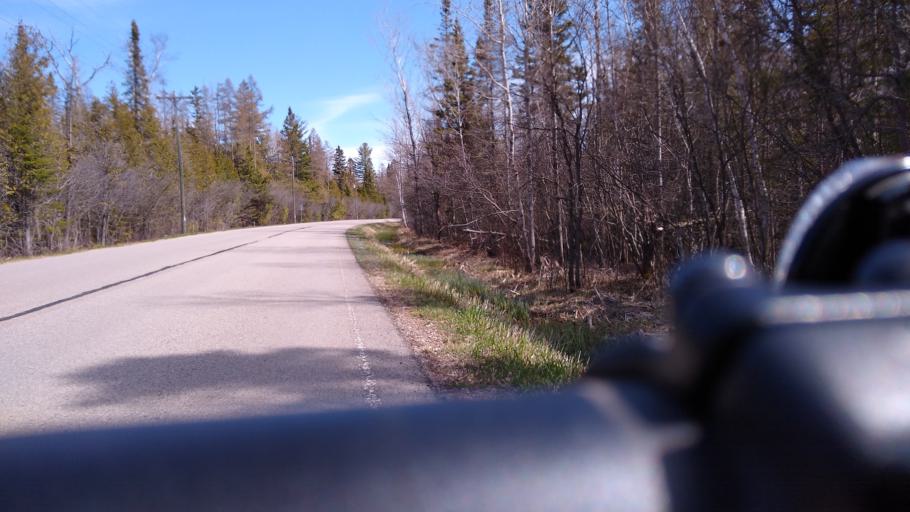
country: US
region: Michigan
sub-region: Delta County
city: Escanaba
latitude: 45.6840
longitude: -87.1476
